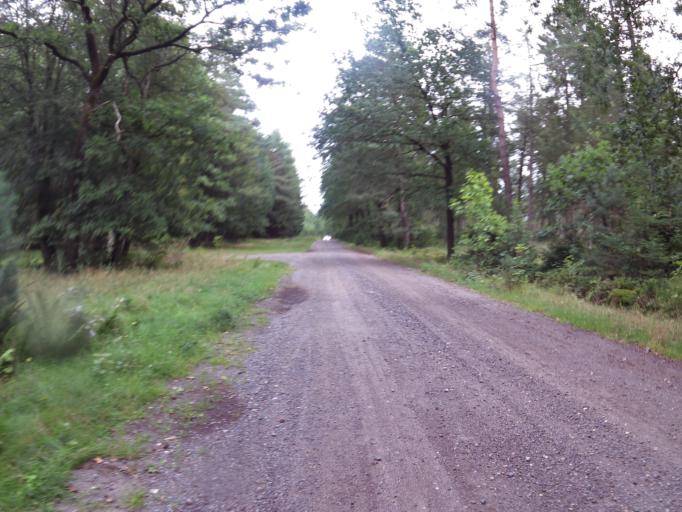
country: DE
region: Lower Saxony
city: Hipstedt
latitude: 53.5010
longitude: 8.9598
